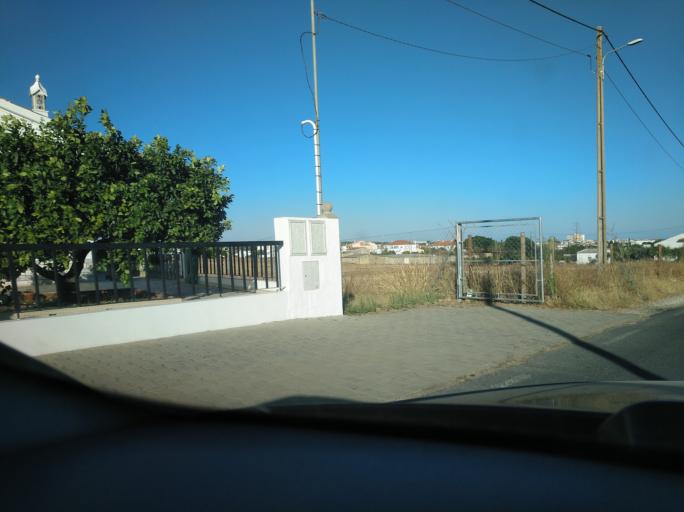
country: PT
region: Faro
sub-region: Vila Real de Santo Antonio
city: Monte Gordo
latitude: 37.1806
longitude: -7.5179
